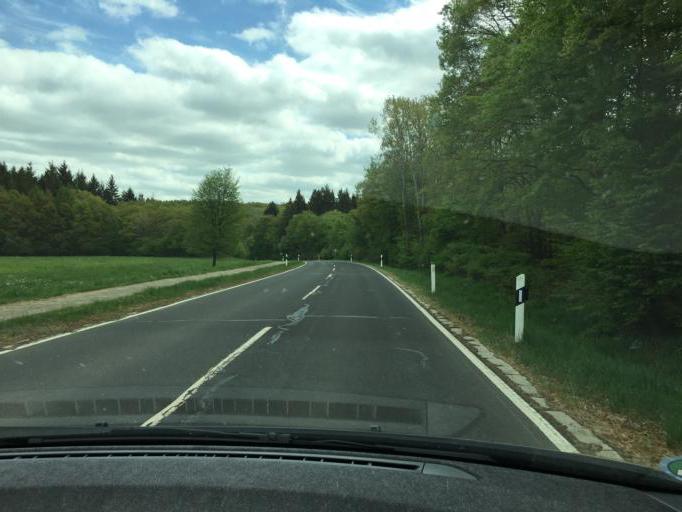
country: DE
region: Rheinland-Pfalz
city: Kirchsahr
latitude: 50.5089
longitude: 6.8849
